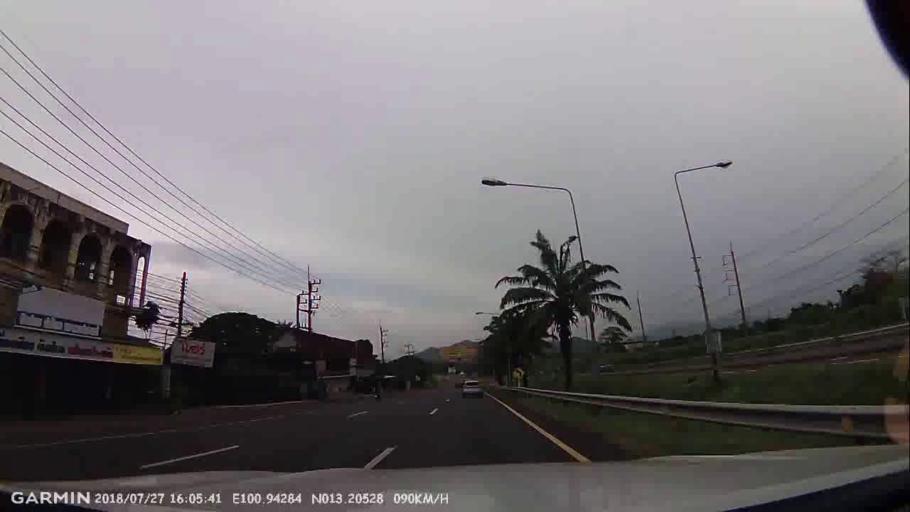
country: TH
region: Chon Buri
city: Si Racha
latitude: 13.2055
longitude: 100.9430
